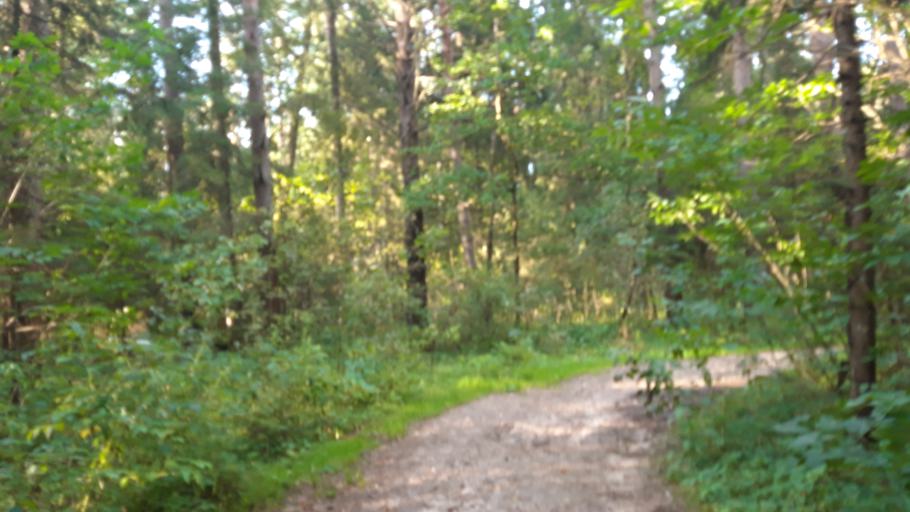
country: RU
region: Tverskaya
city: Konakovo
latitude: 56.6910
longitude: 36.7221
